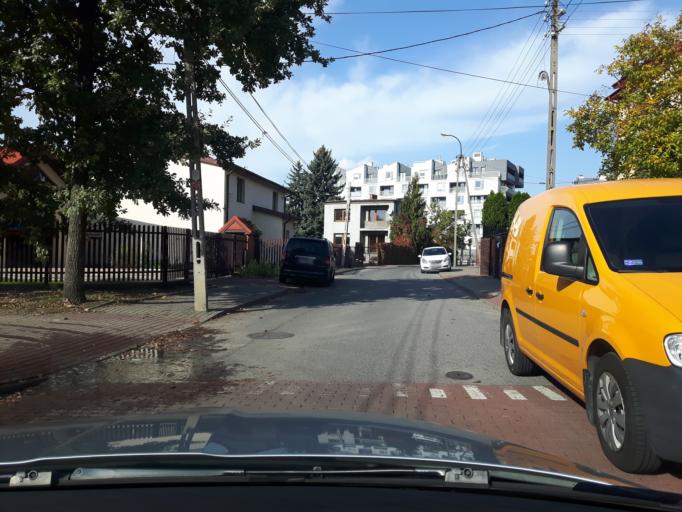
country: PL
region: Masovian Voivodeship
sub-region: Powiat wolominski
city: Zabki
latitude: 52.2859
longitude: 21.0797
